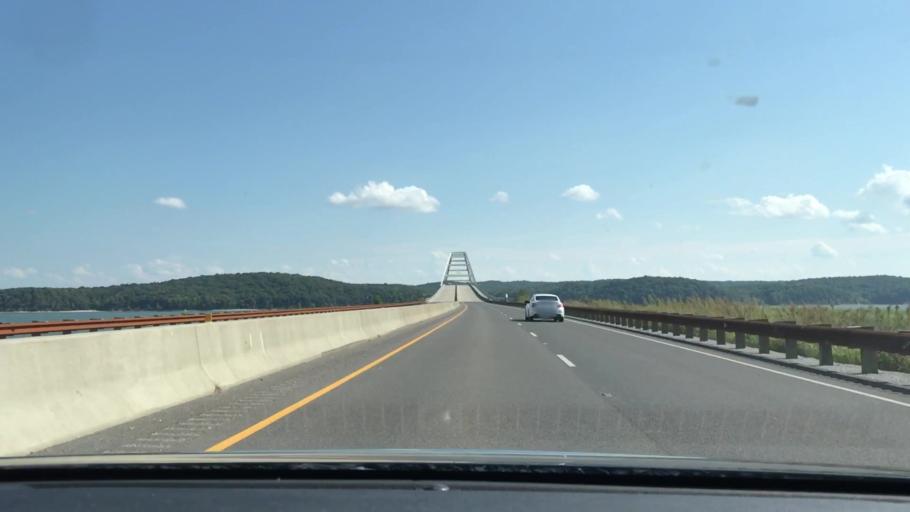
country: US
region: Kentucky
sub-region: Marshall County
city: Benton
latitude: 36.7713
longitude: -88.1293
